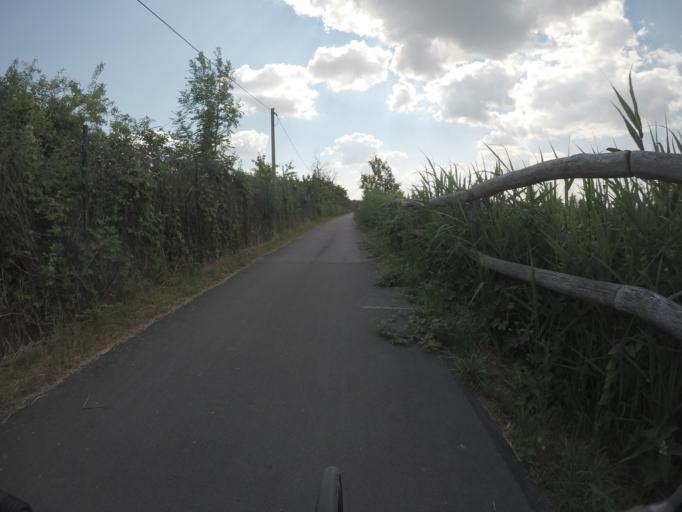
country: DE
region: Brandenburg
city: Roskow
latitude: 52.4556
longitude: 12.7799
